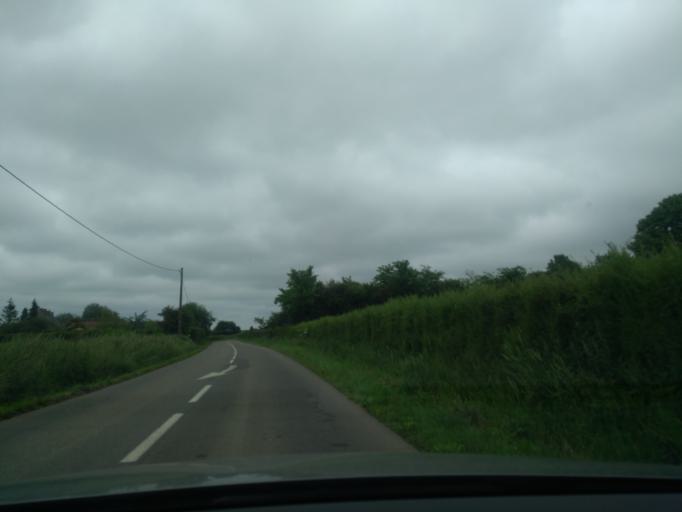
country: FR
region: Lower Normandy
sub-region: Departement de la Manche
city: Sainte-Mere-Eglise
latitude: 49.4318
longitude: -1.2992
